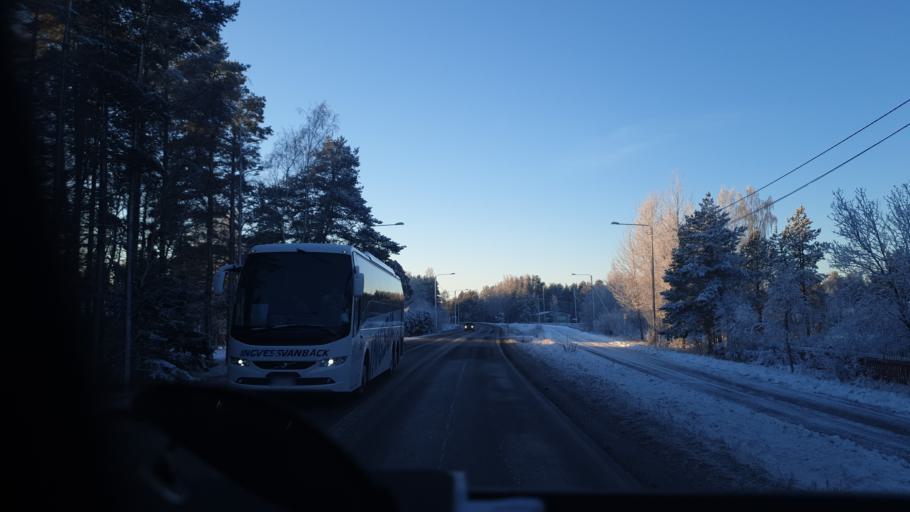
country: FI
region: Northern Ostrobothnia
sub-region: Ylivieska
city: Kalajoki
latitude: 64.2106
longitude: 23.7750
